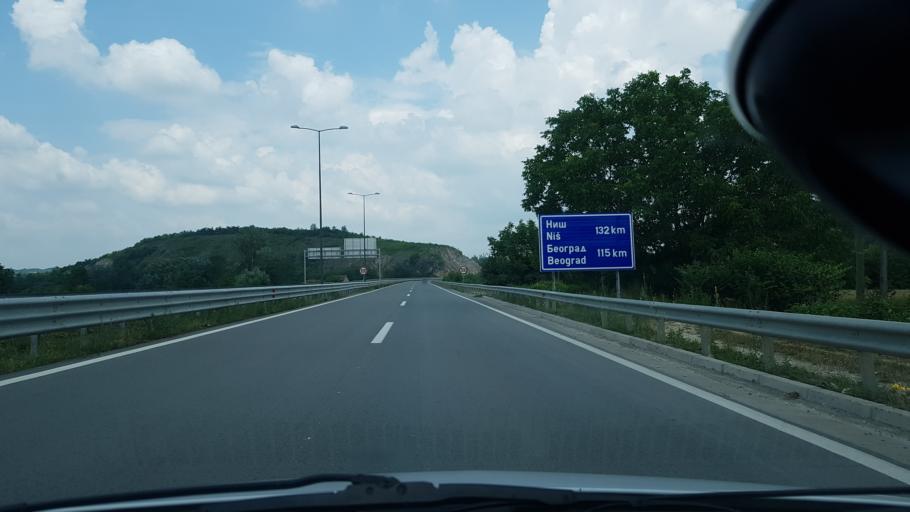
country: RS
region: Central Serbia
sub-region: Sumadijski Okrug
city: Batocina
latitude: 44.1468
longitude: 21.0310
